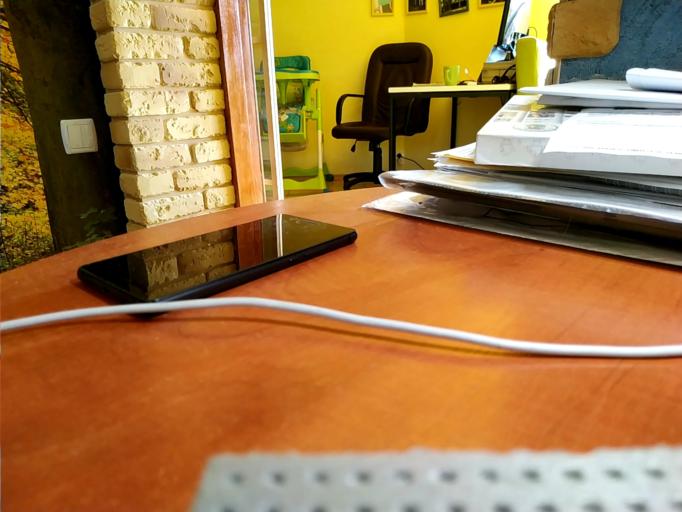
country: RU
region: Tverskaya
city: Kalashnikovo
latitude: 57.3682
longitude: 35.4284
